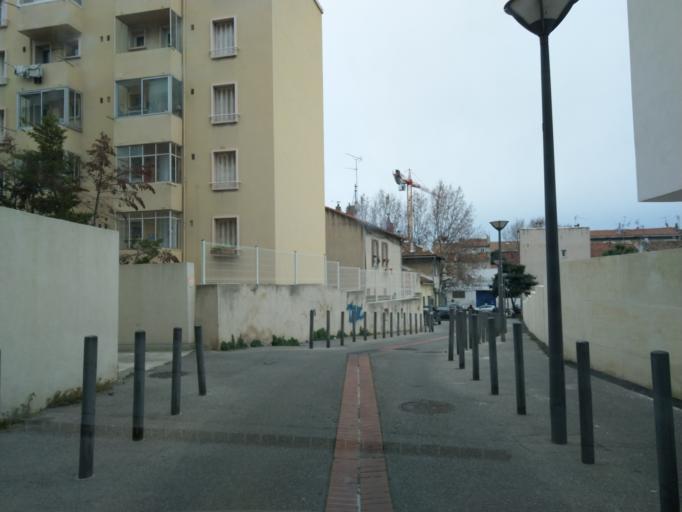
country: FR
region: Provence-Alpes-Cote d'Azur
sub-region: Departement des Bouches-du-Rhone
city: Marseille 08
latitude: 43.2801
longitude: 5.3924
